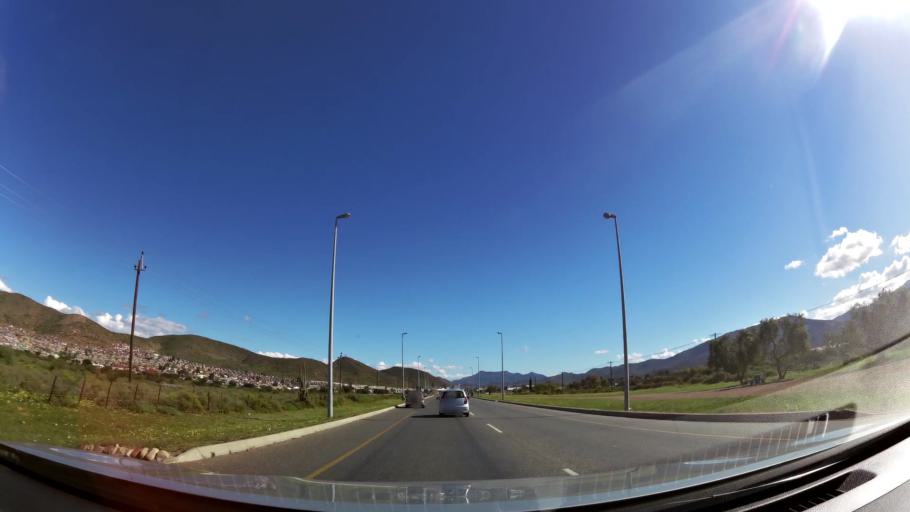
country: ZA
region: Western Cape
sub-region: Cape Winelands District Municipality
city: Ashton
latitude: -33.8148
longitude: 19.9009
